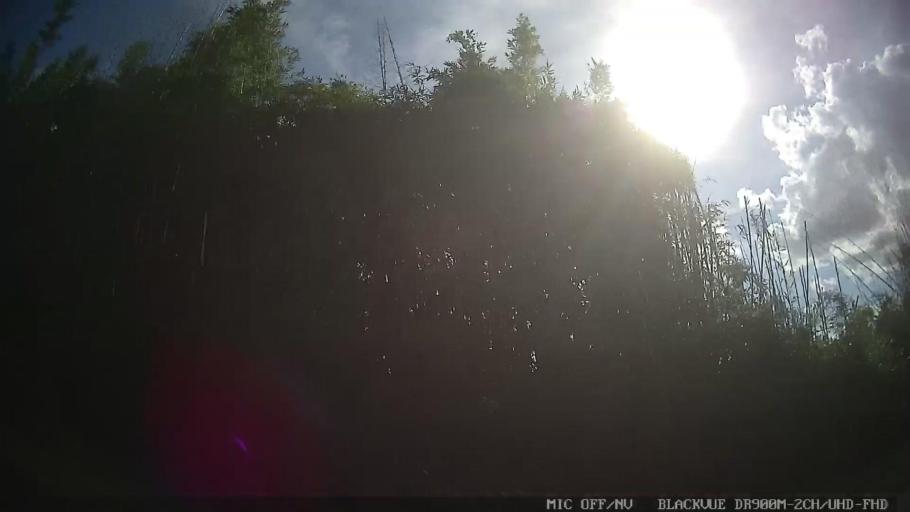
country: BR
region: Sao Paulo
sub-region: Laranjal Paulista
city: Laranjal Paulista
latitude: -23.0420
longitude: -47.8281
